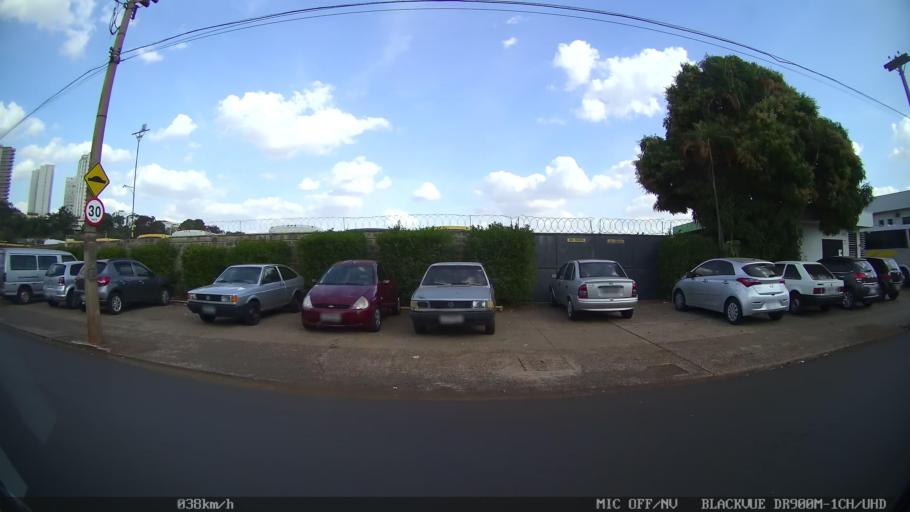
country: BR
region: Sao Paulo
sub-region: Ribeirao Preto
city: Ribeirao Preto
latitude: -21.1783
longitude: -47.8194
